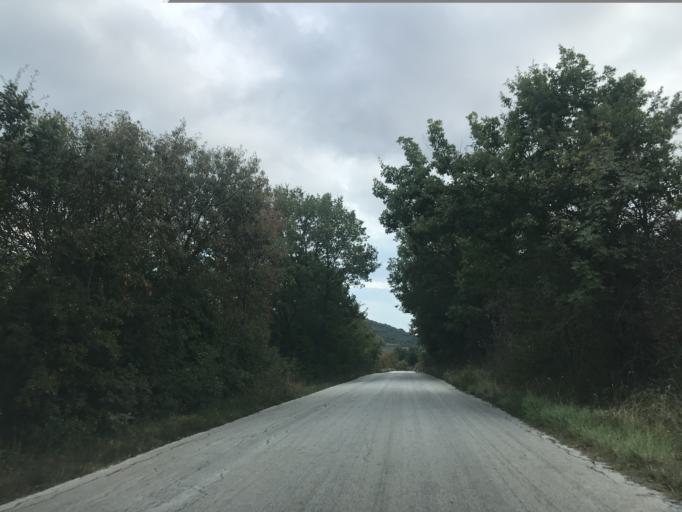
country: IT
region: Molise
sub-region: Provincia di Campobasso
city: Duronia
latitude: 41.6783
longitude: 14.4533
